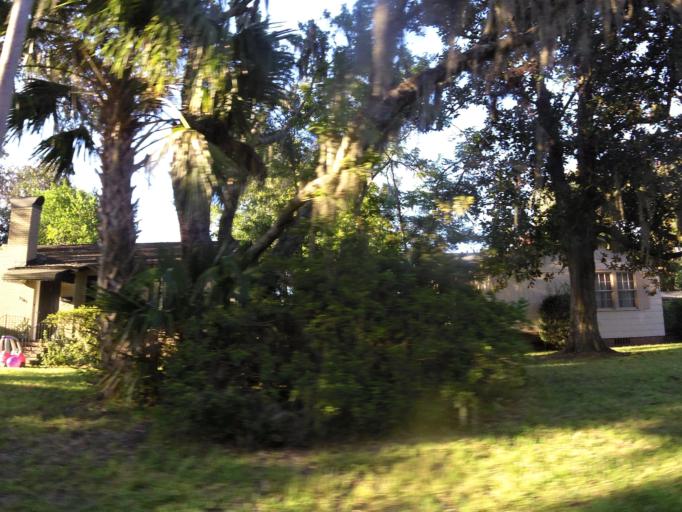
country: US
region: Florida
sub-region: Duval County
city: Jacksonville
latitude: 30.2825
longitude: -81.6476
